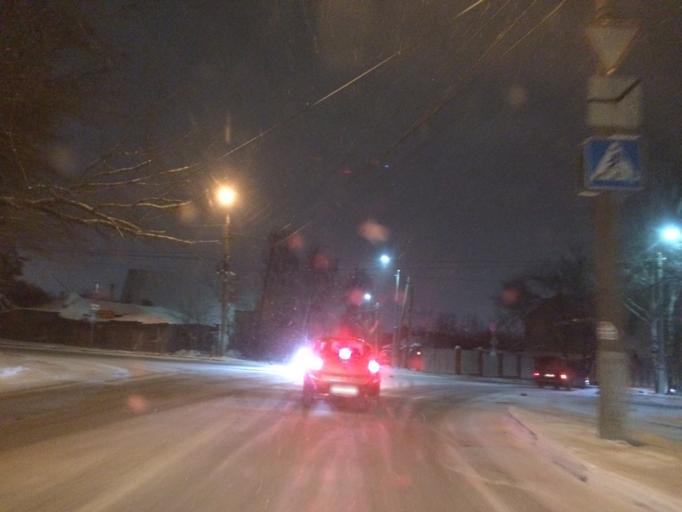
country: RU
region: Tula
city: Tula
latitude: 54.1799
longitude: 37.6166
